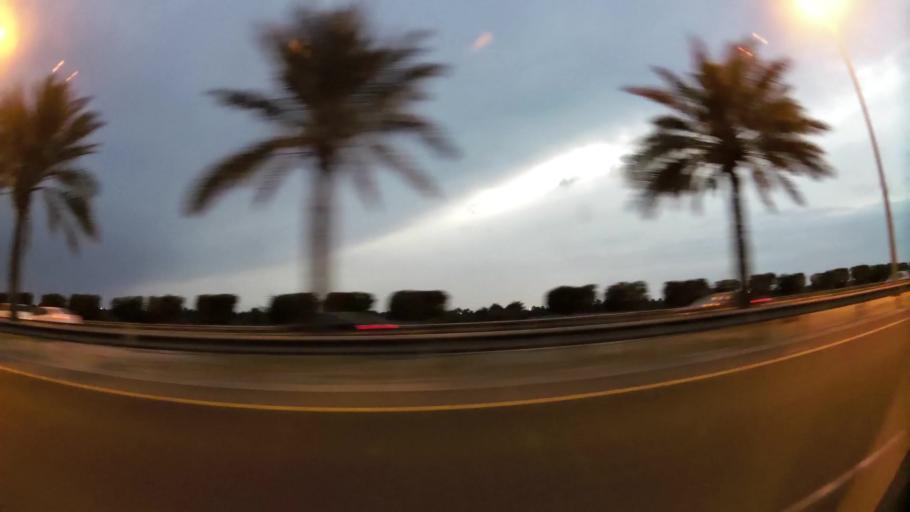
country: BH
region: Central Governorate
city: Madinat Hamad
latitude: 26.1568
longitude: 50.5061
